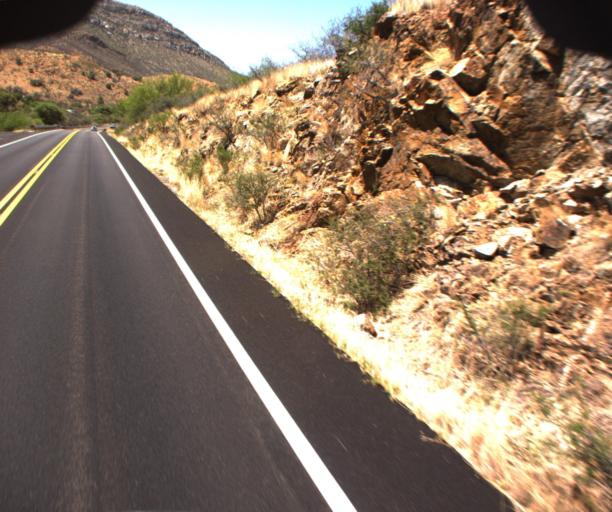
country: US
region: Arizona
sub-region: Cochise County
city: Bisbee
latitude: 31.4974
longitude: -109.9975
